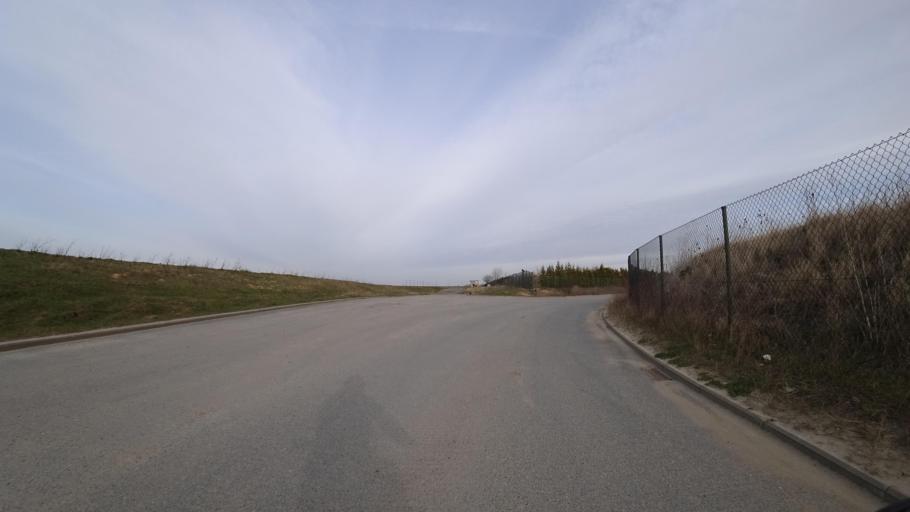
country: BE
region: Wallonia
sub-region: Province du Brabant Wallon
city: Chaumont-Gistoux
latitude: 50.6707
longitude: 4.7120
